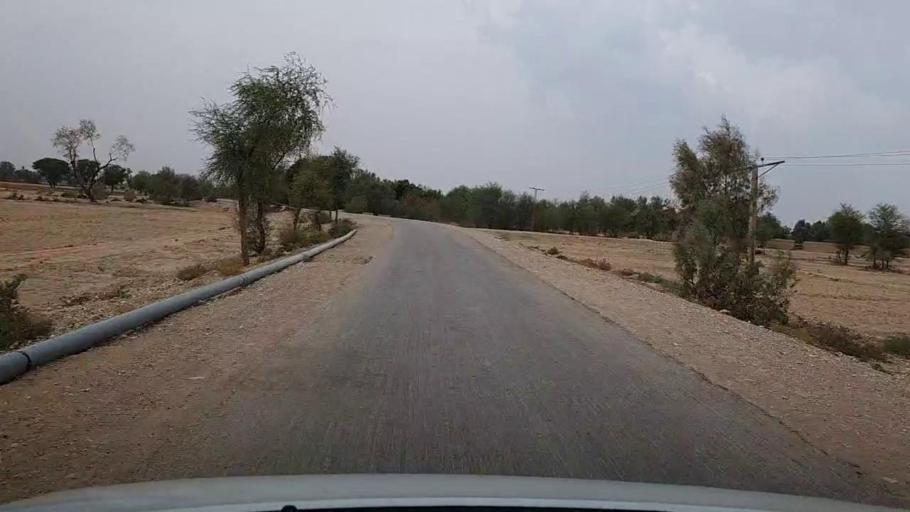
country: PK
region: Sindh
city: Sehwan
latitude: 26.3213
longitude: 67.7314
